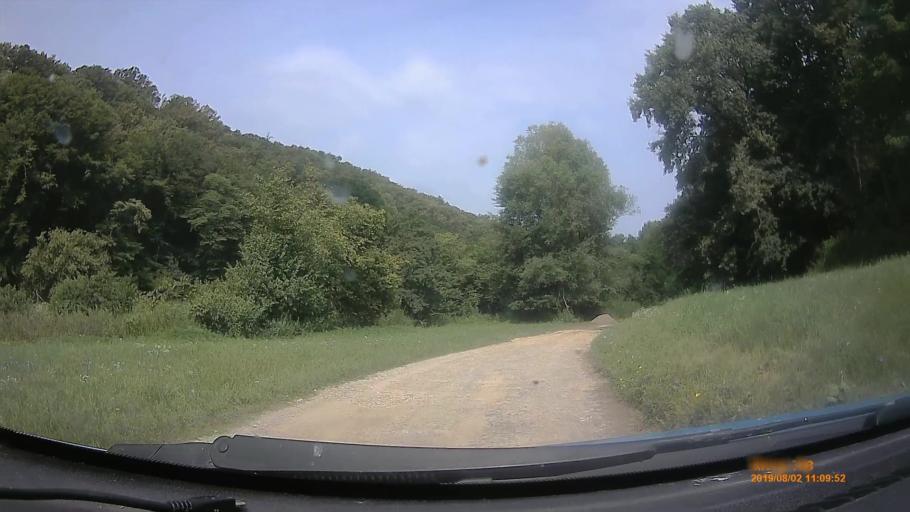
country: HU
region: Baranya
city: Buekkoesd
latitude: 46.1033
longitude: 17.9385
